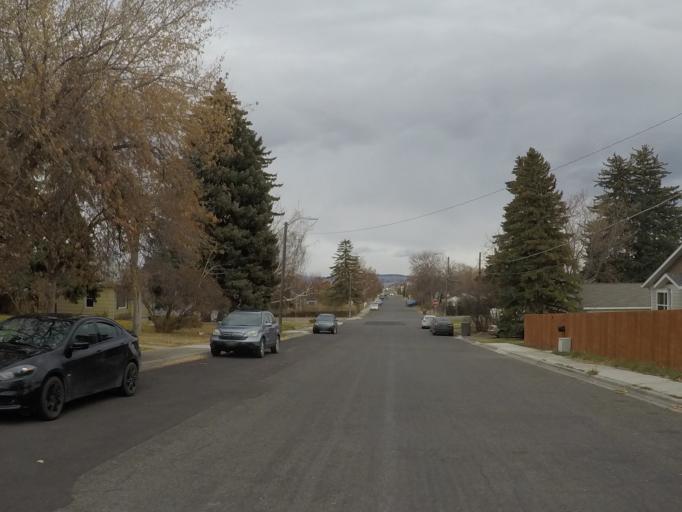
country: US
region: Montana
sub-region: Lewis and Clark County
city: Helena
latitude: 46.5910
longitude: -112.0252
